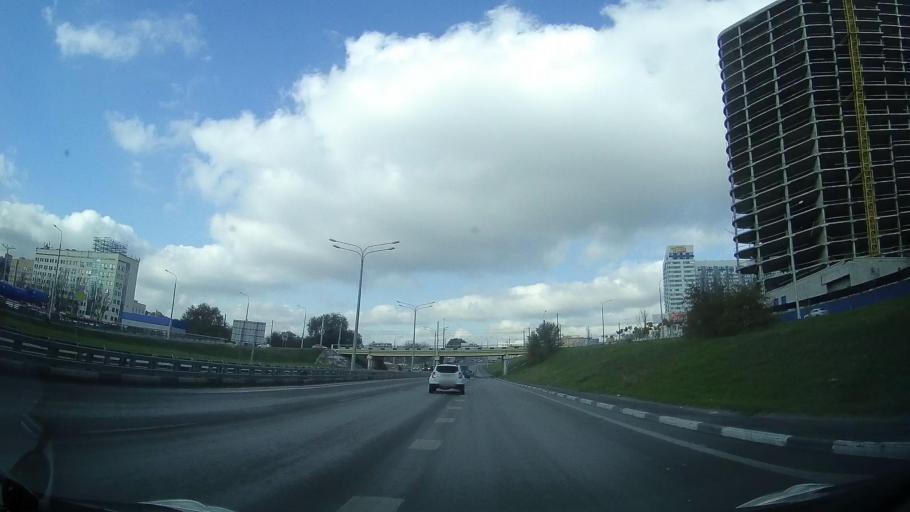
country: RU
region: Rostov
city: Rostov-na-Donu
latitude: 47.2214
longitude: 39.6934
